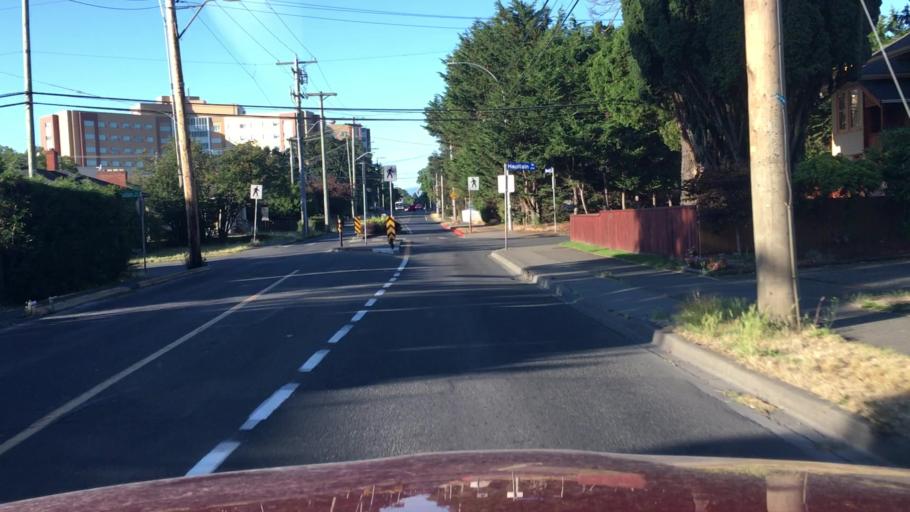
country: CA
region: British Columbia
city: Oak Bay
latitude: 48.4363
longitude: -123.3287
